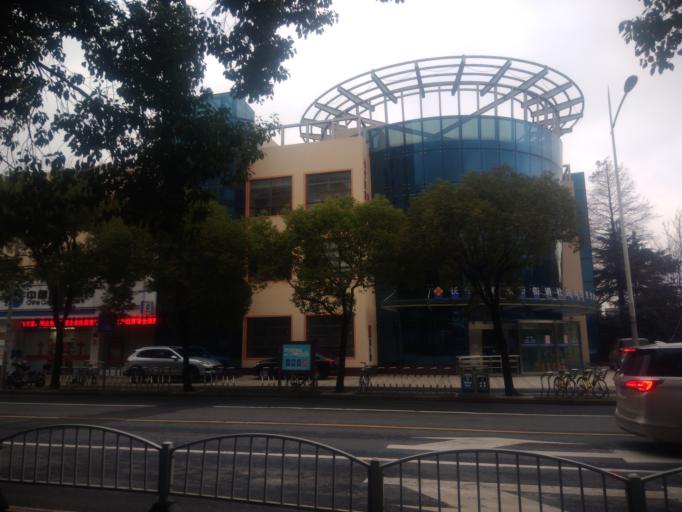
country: CN
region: Shanghai Shi
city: Changzheng
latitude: 31.1933
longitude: 121.3707
